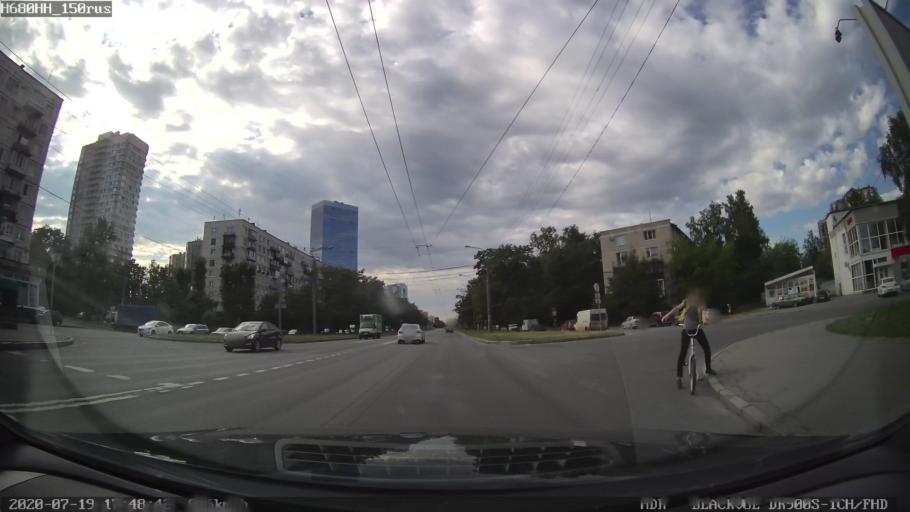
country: RU
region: St.-Petersburg
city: Kupchino
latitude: 59.8482
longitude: 30.3118
